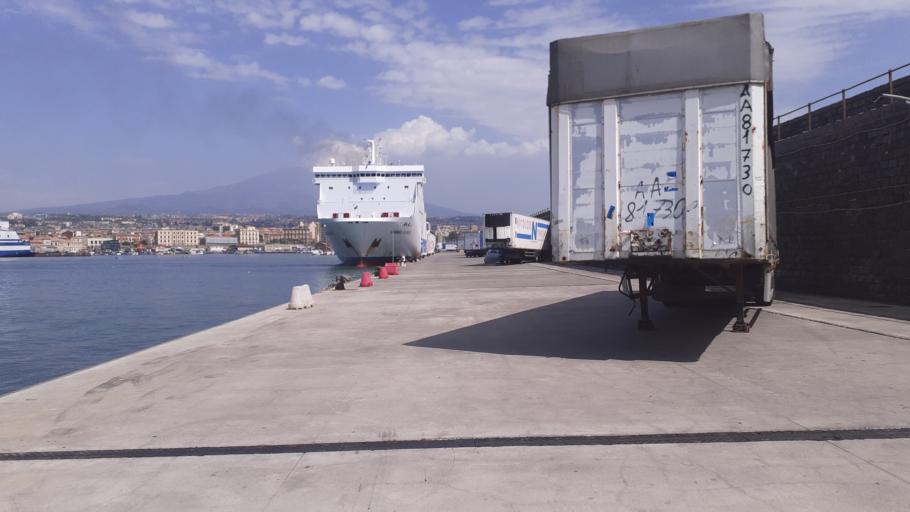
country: IT
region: Sicily
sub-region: Catania
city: Catania
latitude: 37.4944
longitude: 15.0995
